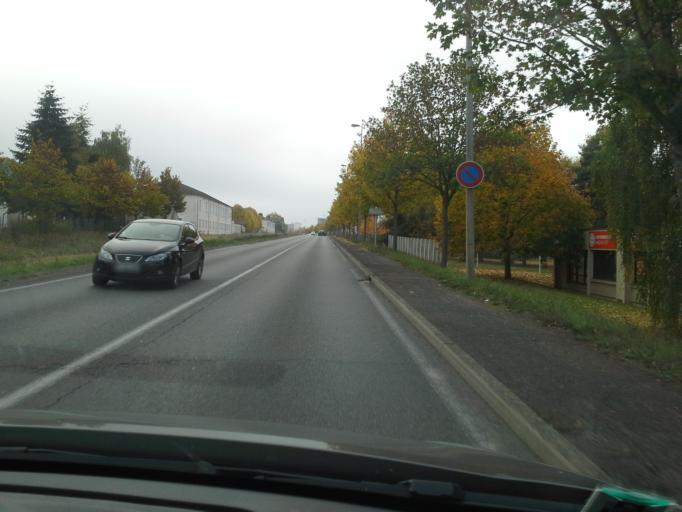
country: FR
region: Centre
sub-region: Departement d'Indre-et-Loire
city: Chanceaux-sur-Choisille
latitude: 47.4361
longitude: 0.7089
